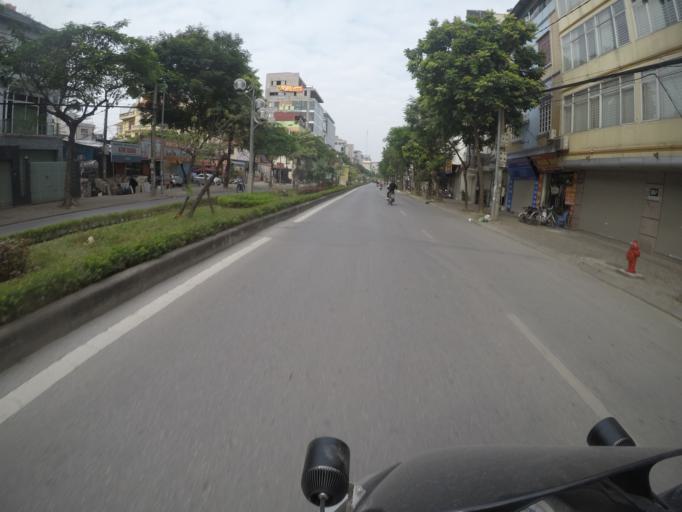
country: VN
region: Ha Noi
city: Tay Ho
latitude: 21.0635
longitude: 105.8096
